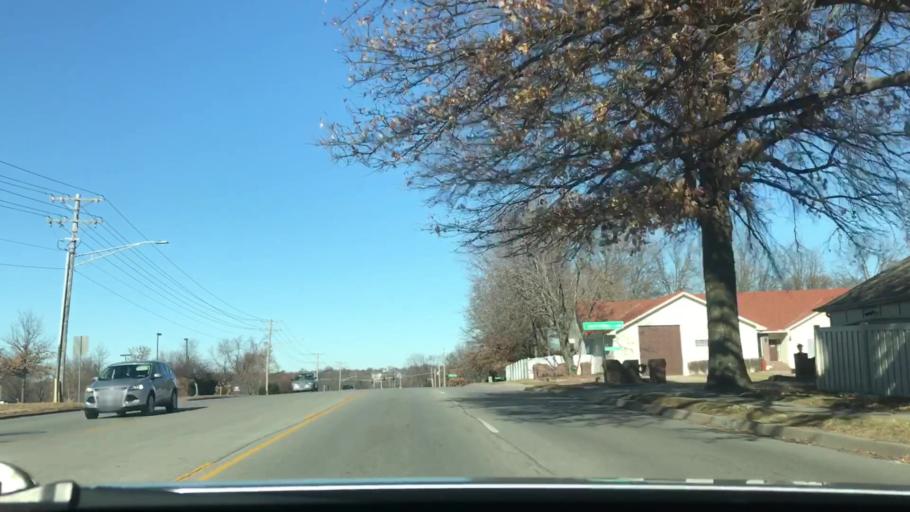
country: US
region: Missouri
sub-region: Jackson County
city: Independence
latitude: 39.0522
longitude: -94.3871
